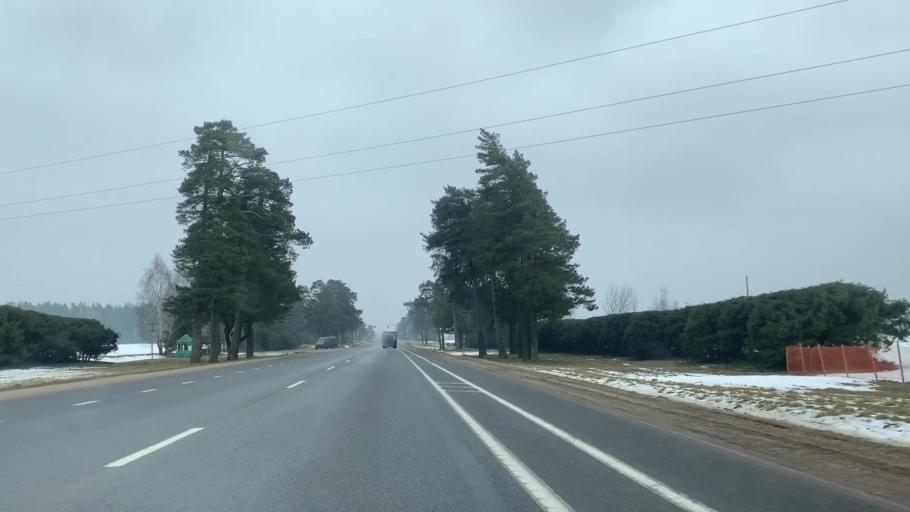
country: BY
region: Minsk
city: Nyasvizh
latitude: 53.2494
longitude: 26.6223
